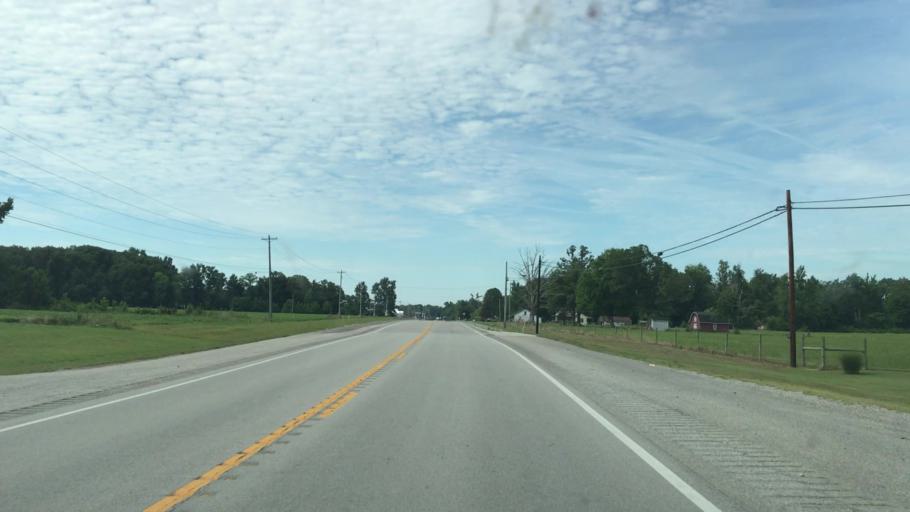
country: US
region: Kentucky
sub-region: Edmonson County
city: Brownsville
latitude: 37.1399
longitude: -86.2306
